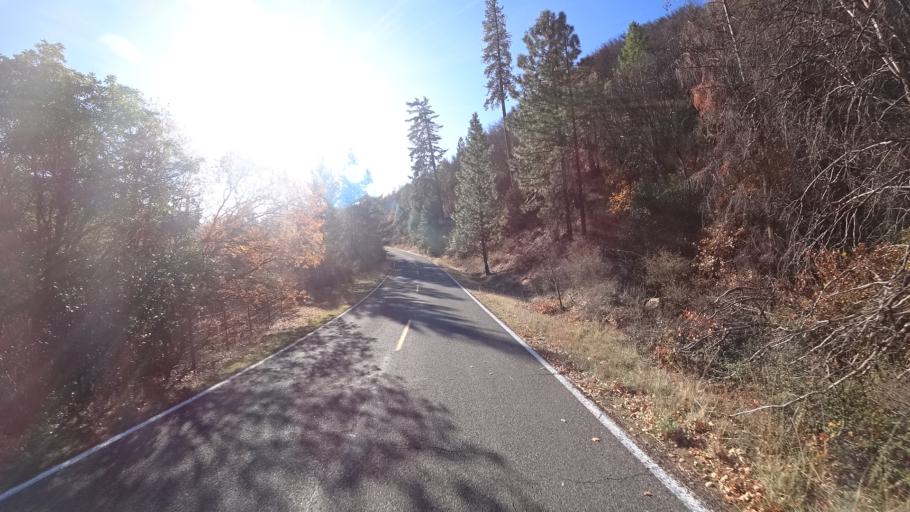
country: US
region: California
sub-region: Siskiyou County
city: Yreka
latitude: 41.9095
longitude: -122.8363
